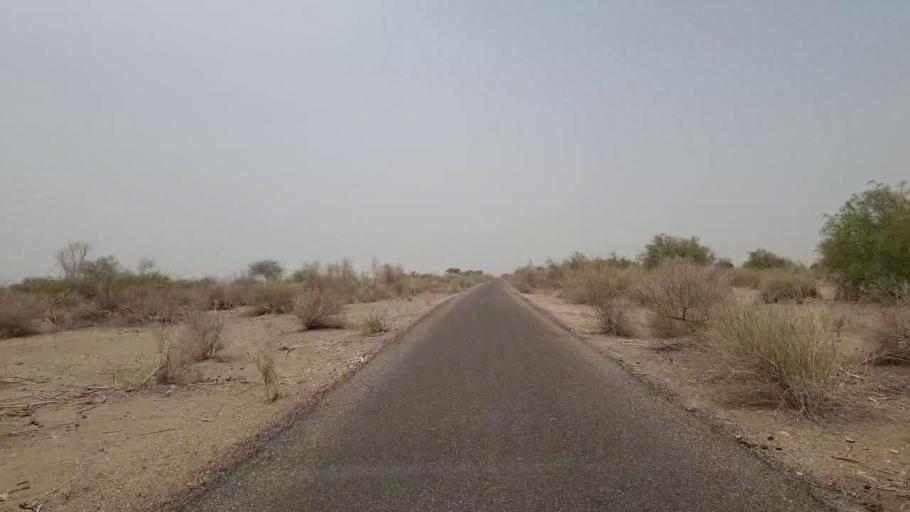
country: PK
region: Sindh
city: Islamkot
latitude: 24.7652
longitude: 70.4805
